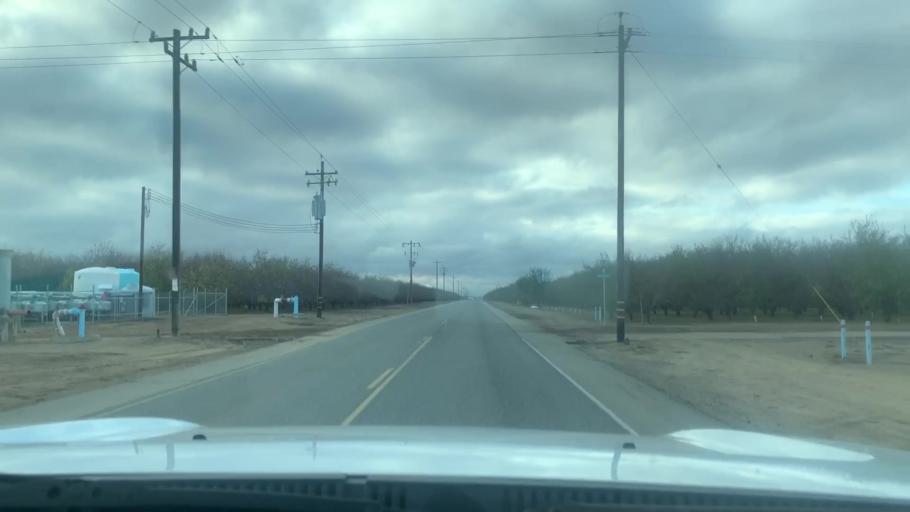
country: US
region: California
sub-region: Kern County
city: Buttonwillow
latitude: 35.5007
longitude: -119.5102
